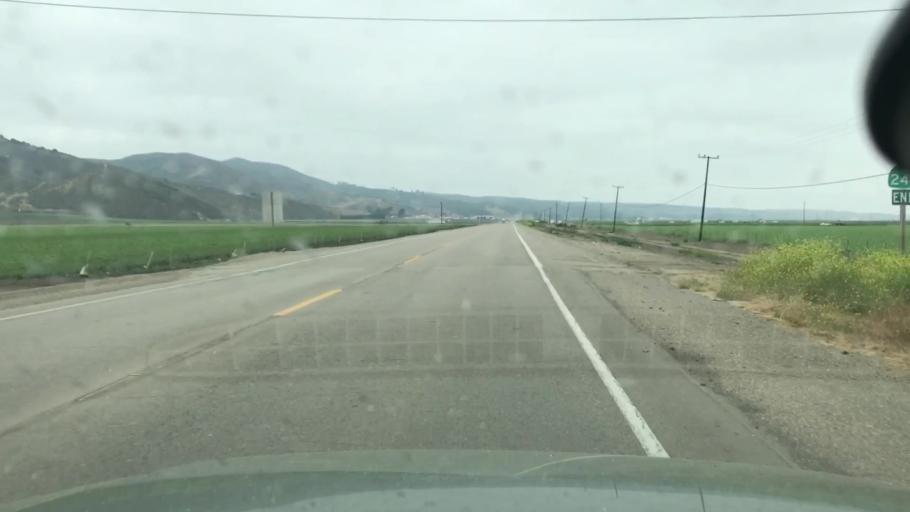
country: US
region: California
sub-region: Santa Barbara County
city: Lompoc
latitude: 34.6391
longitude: -120.4794
